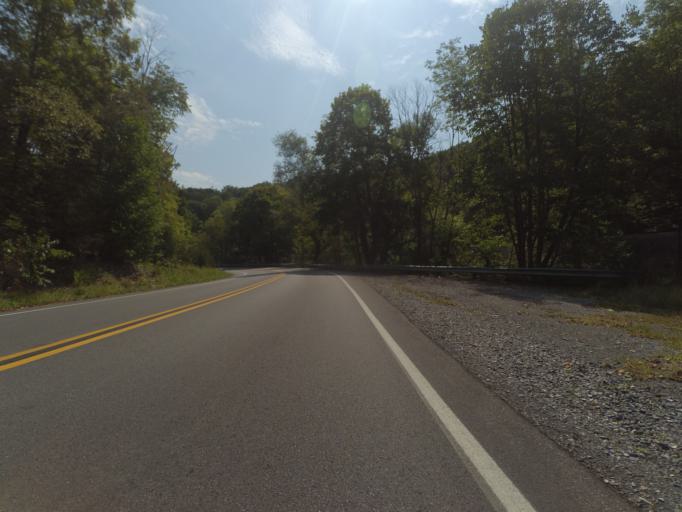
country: US
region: Pennsylvania
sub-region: Centre County
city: Bellefonte
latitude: 40.8914
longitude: -77.7672
